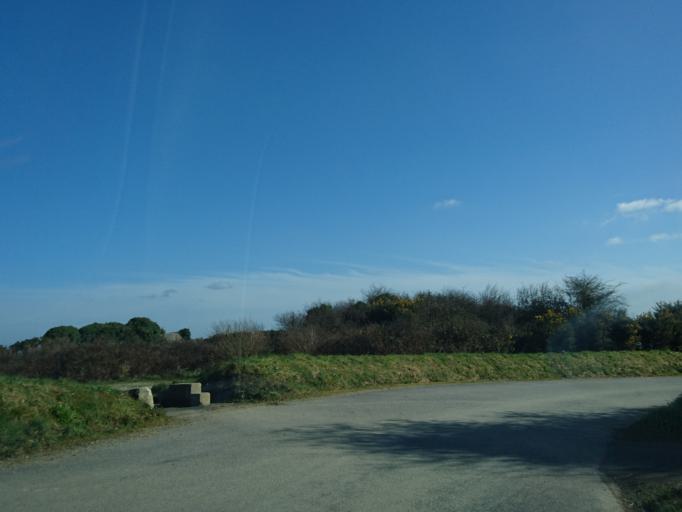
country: FR
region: Brittany
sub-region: Departement du Finistere
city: Roscanvel
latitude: 48.3403
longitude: -4.5353
